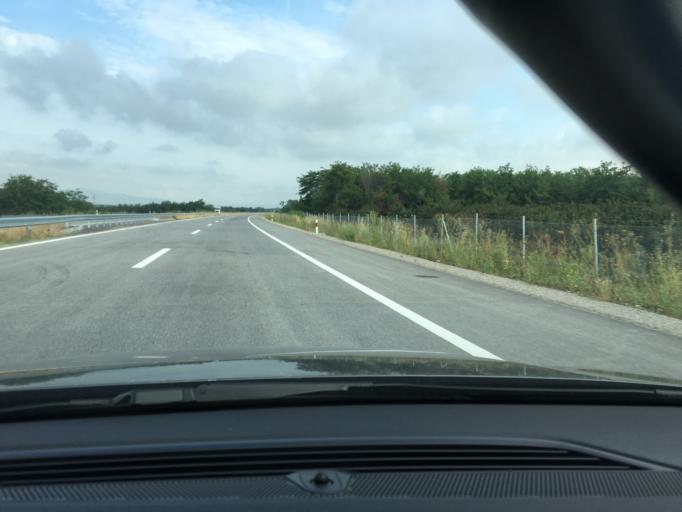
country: MK
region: Sveti Nikole
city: Sveti Nikole
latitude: 41.8339
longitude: 21.9900
